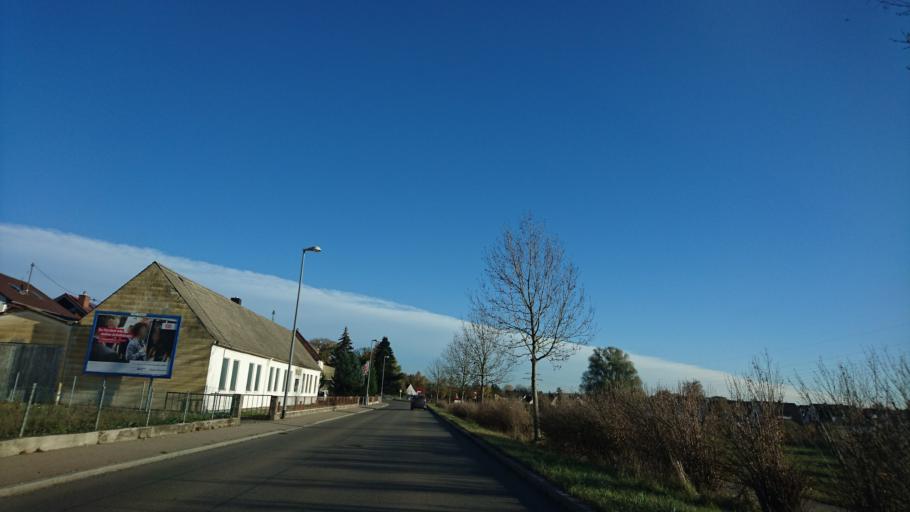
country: DE
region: Bavaria
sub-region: Swabia
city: Dinkelscherben
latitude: 48.3495
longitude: 10.5825
